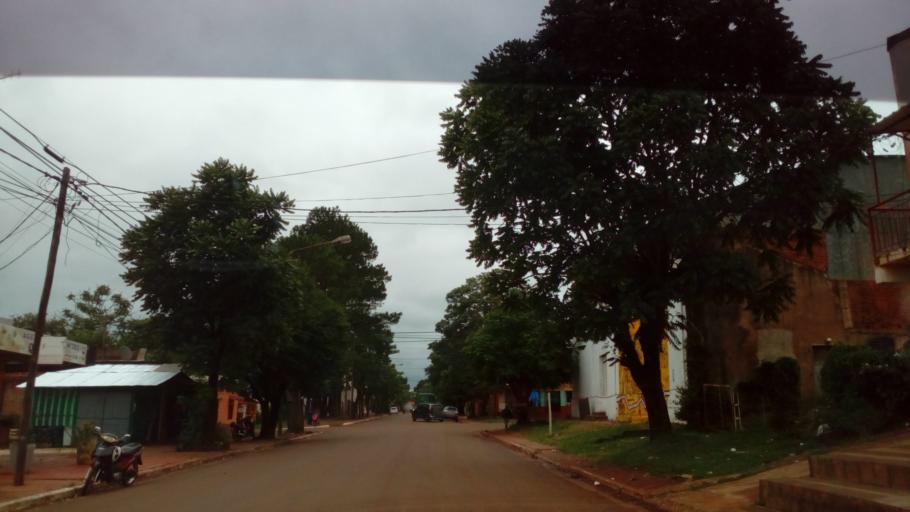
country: AR
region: Misiones
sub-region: Departamento de Candelaria
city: Candelaria
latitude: -27.4603
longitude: -55.7467
